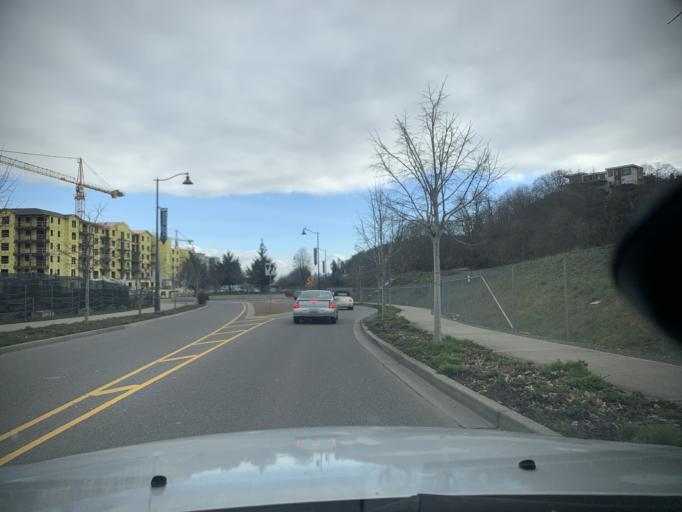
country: US
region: Washington
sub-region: Pierce County
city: Fircrest
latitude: 47.2982
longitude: -122.5066
